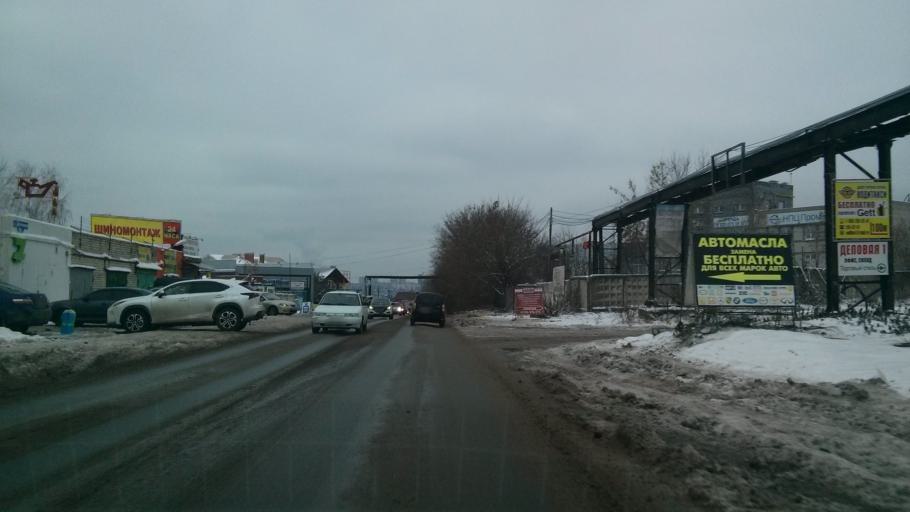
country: RU
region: Nizjnij Novgorod
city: Afonino
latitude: 56.3056
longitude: 44.0674
